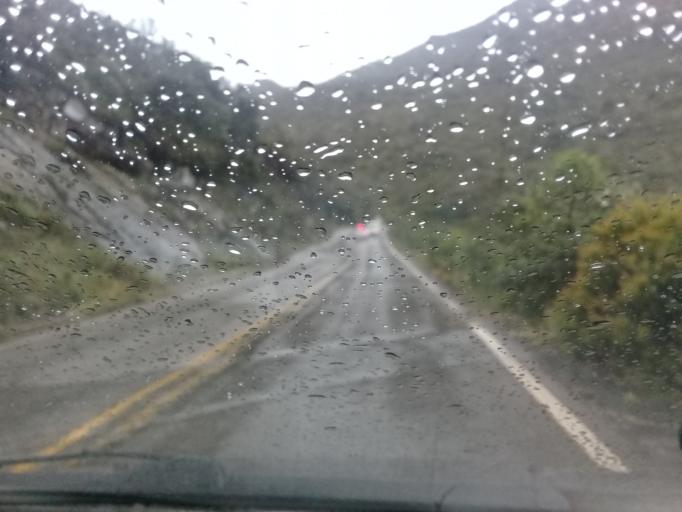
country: CO
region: Cundinamarca
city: Guasca
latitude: 4.8423
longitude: -73.8130
